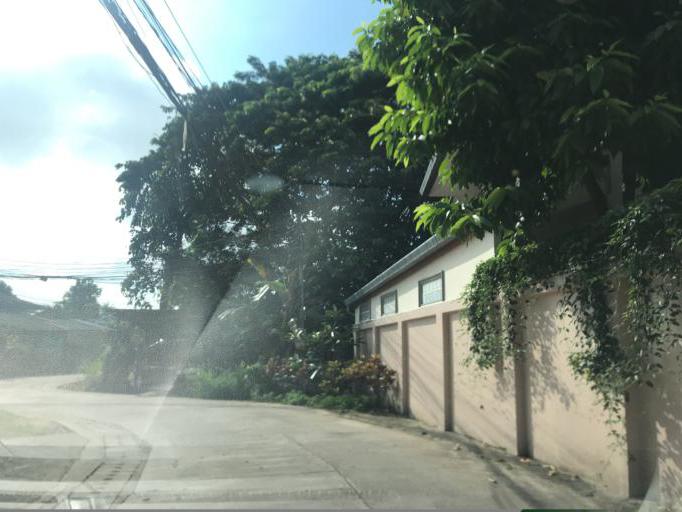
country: TH
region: Chiang Mai
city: San Sai
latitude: 18.8285
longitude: 99.0218
